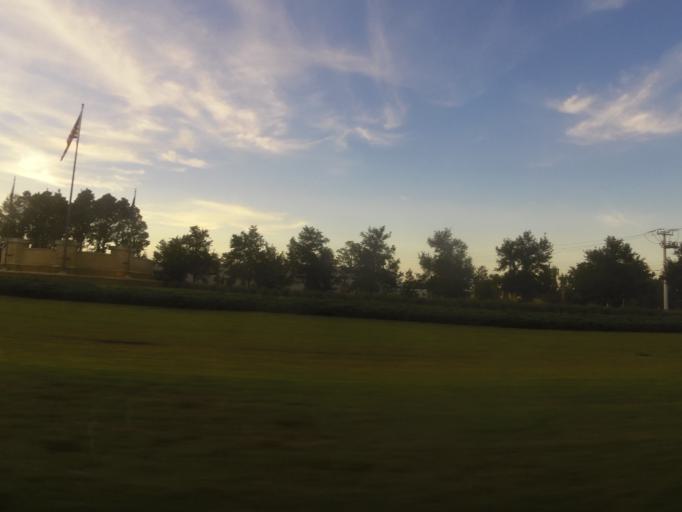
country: US
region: Florida
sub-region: Saint Johns County
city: Palm Valley
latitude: 30.1230
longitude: -81.4001
